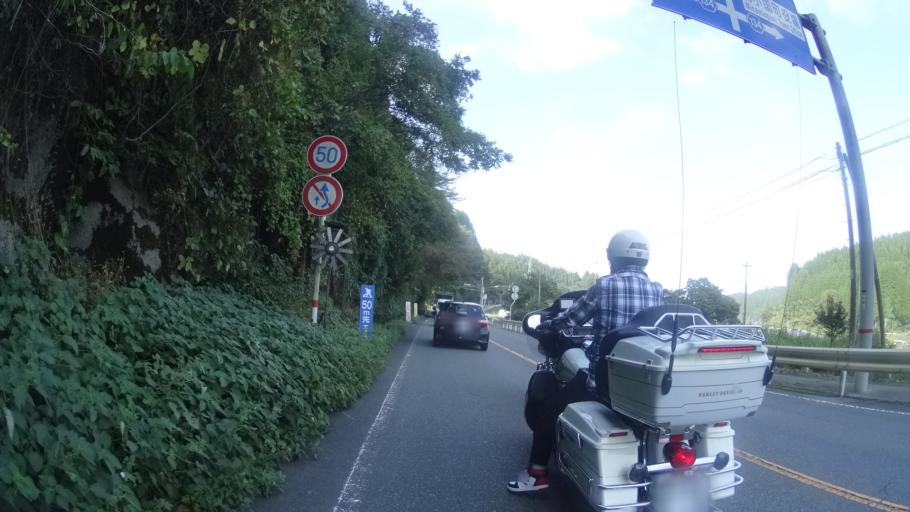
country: JP
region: Kumamoto
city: Aso
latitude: 33.0920
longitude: 131.0668
